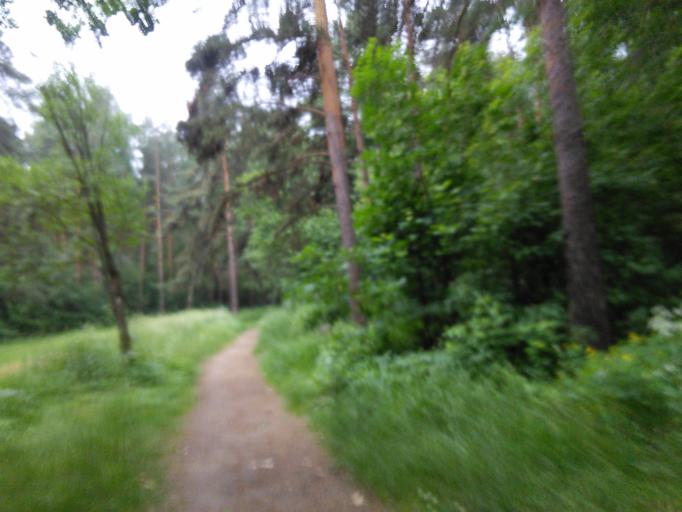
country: RU
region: Moskovskaya
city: Dzerzhinskiy
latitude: 55.6420
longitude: 37.8753
